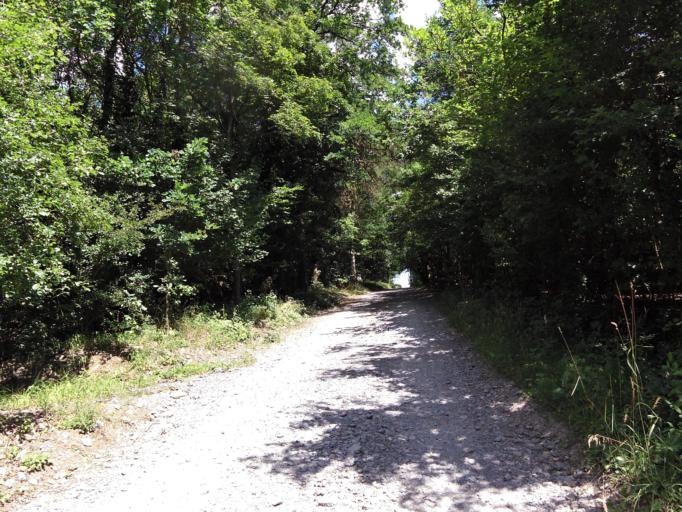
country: DE
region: Bavaria
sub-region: Regierungsbezirk Unterfranken
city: Gadheim
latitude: 49.8315
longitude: 9.9224
